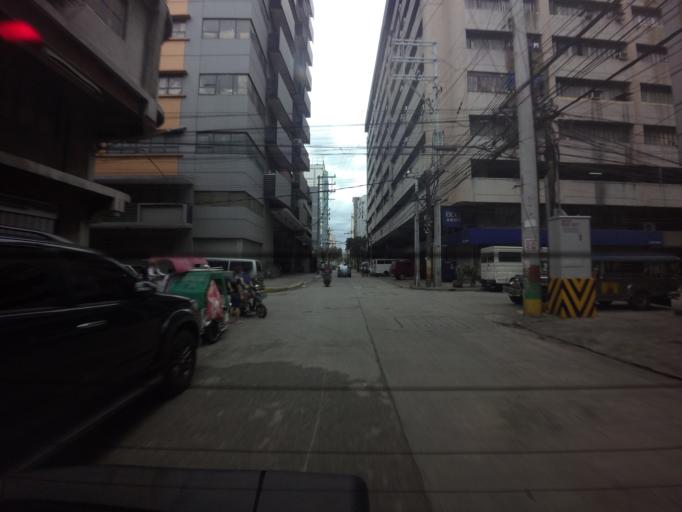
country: PH
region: Metro Manila
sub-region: City of Manila
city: Manila
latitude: 14.6015
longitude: 120.9689
